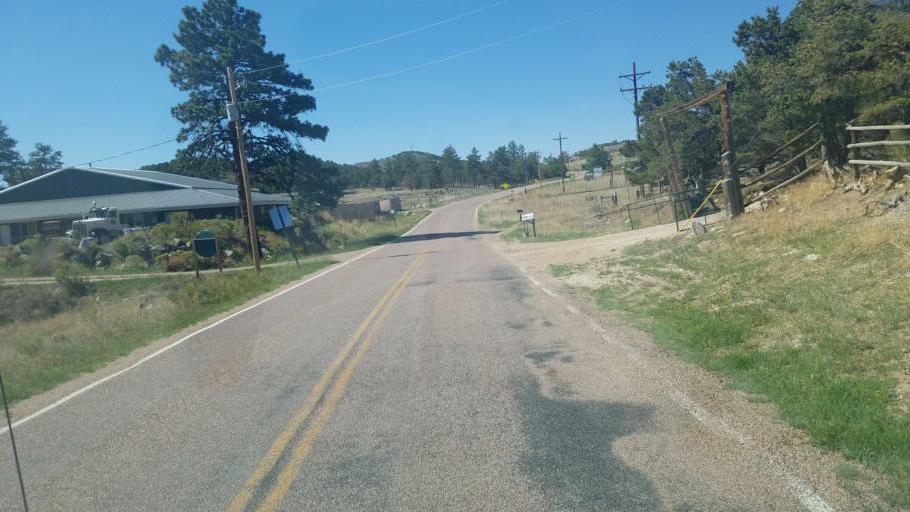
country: US
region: Colorado
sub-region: Custer County
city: Westcliffe
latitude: 38.3391
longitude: -105.4851
